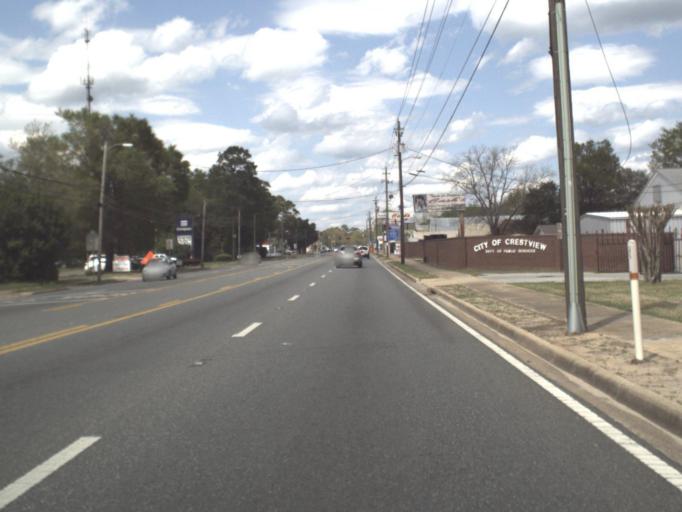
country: US
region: Florida
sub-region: Okaloosa County
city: Crestview
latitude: 30.7698
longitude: -86.5664
